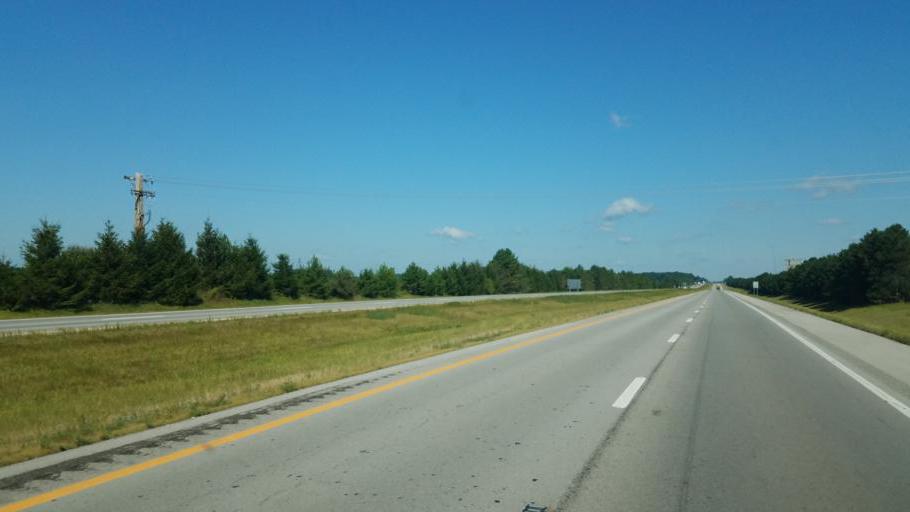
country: US
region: Ohio
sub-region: Wyandot County
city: Upper Sandusky
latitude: 40.8634
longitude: -83.3236
